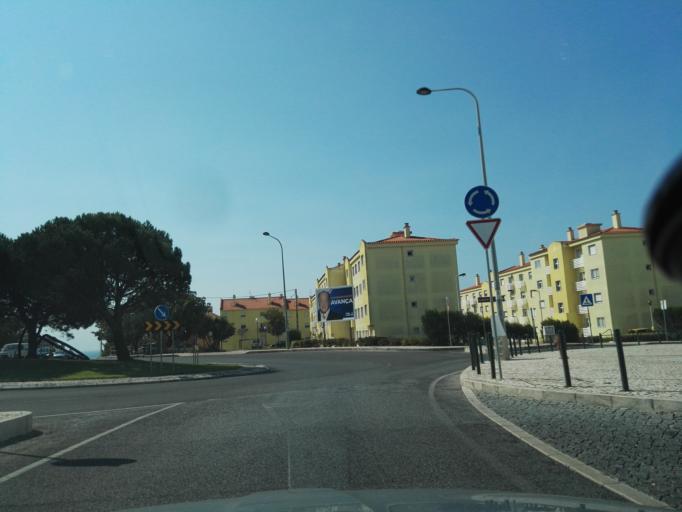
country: PT
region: Lisbon
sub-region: Cascais
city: Estoril
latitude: 38.7096
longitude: -9.3864
